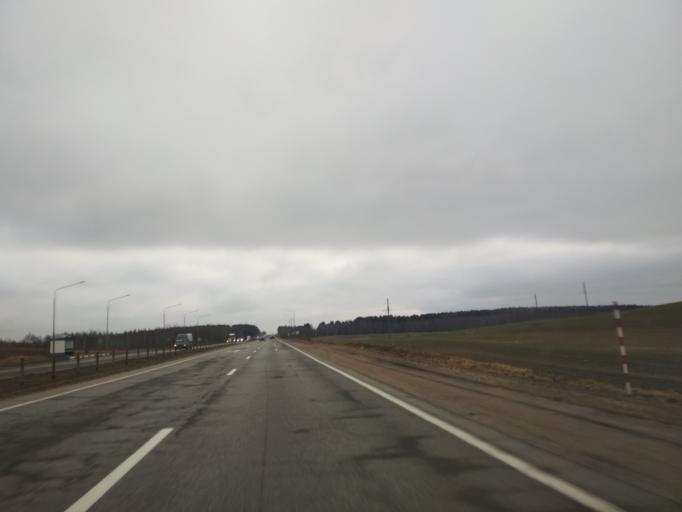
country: BY
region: Minsk
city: Luhavaya Slabada
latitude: 53.7247
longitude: 27.8587
